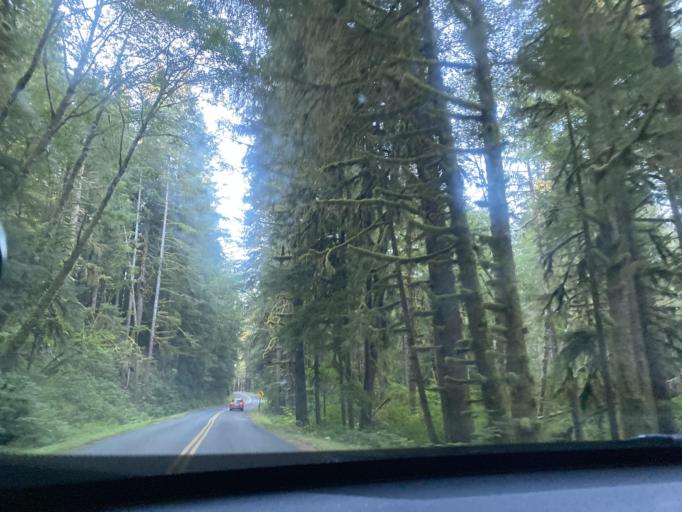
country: US
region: Washington
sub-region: Clallam County
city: Forks
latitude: 47.8119
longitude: -124.1035
